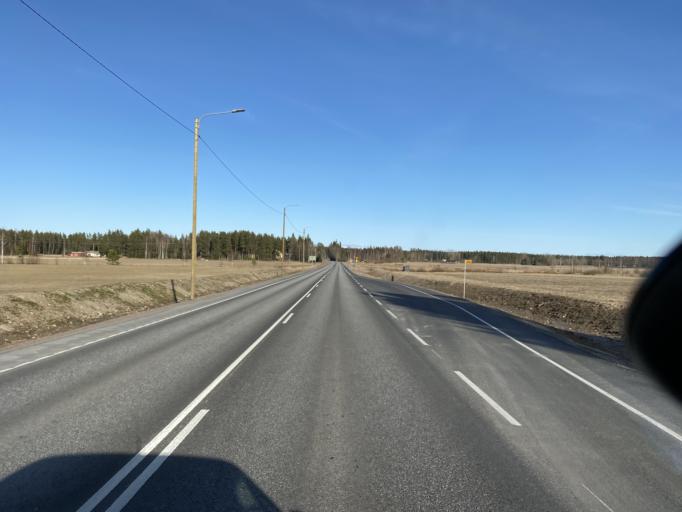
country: FI
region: Satakunta
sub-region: Rauma
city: Koeylioe
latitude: 61.1627
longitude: 22.3176
